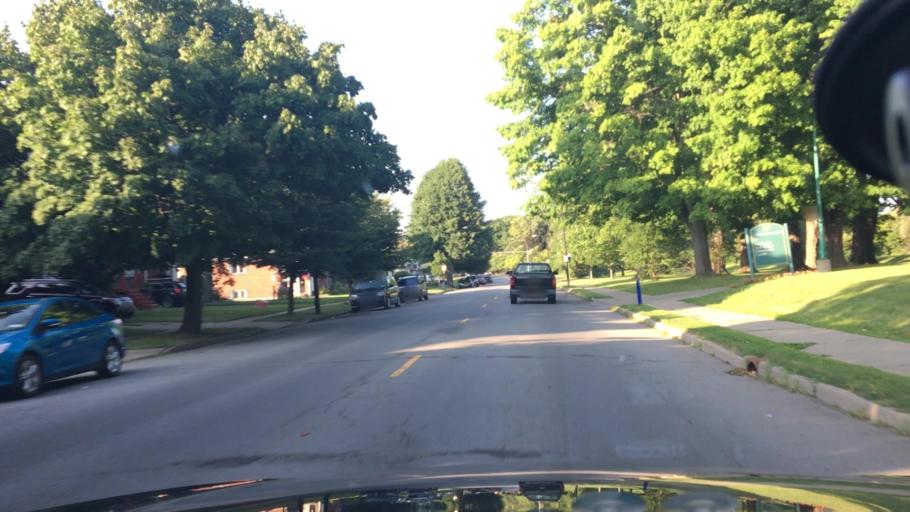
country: US
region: New York
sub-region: Erie County
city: West Seneca
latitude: 42.8491
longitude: -78.8115
